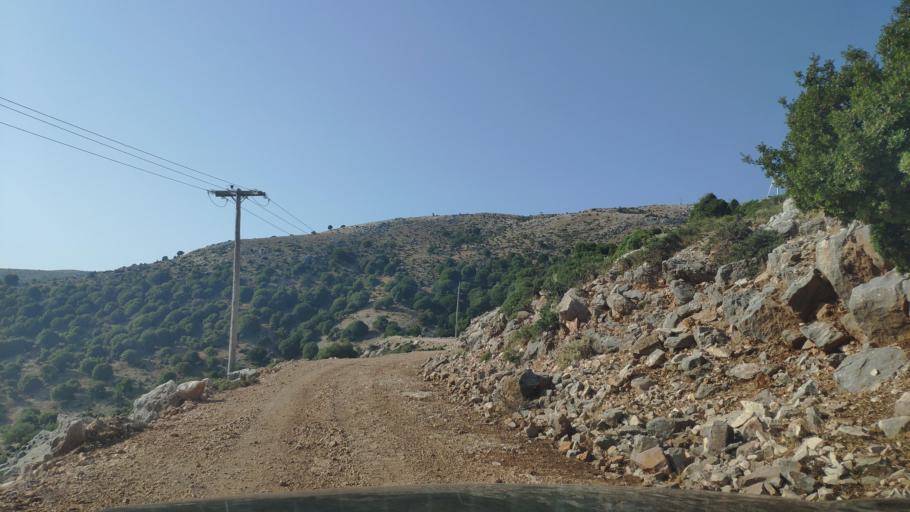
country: GR
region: West Greece
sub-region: Nomos Aitolias kai Akarnanias
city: Monastirakion
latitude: 38.8252
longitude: 20.9799
